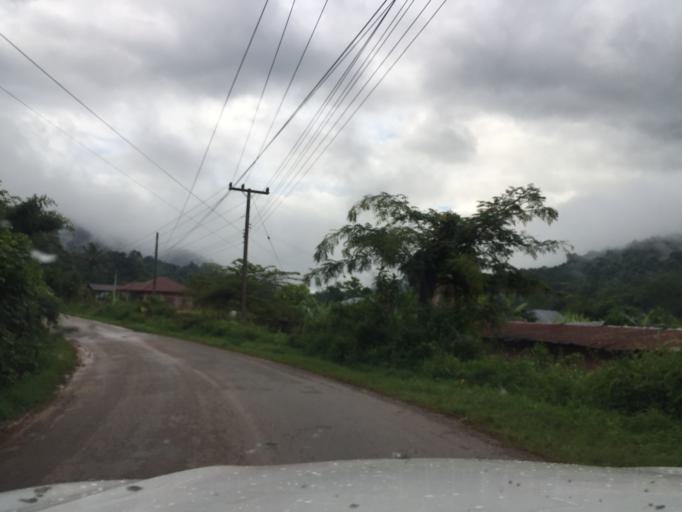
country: LA
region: Oudomxai
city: Muang La
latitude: 20.8491
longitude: 102.1058
